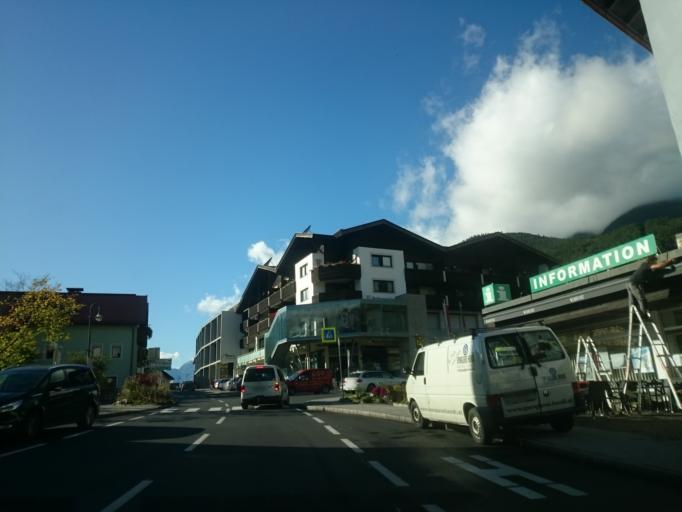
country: AT
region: Tyrol
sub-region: Politischer Bezirk Innsbruck Land
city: Unterperfuss
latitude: 47.2736
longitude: 11.2418
